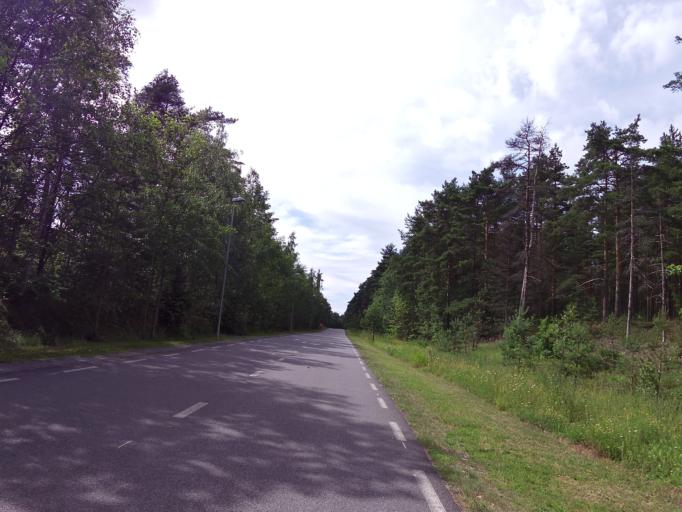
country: EE
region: Harju
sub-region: Saue vald
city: Laagri
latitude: 59.3838
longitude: 24.6472
